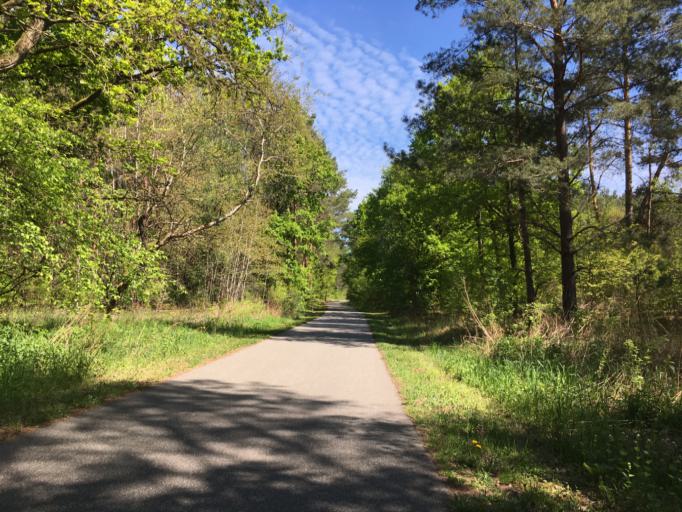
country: DE
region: Brandenburg
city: Bernau bei Berlin
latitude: 52.6871
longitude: 13.5360
